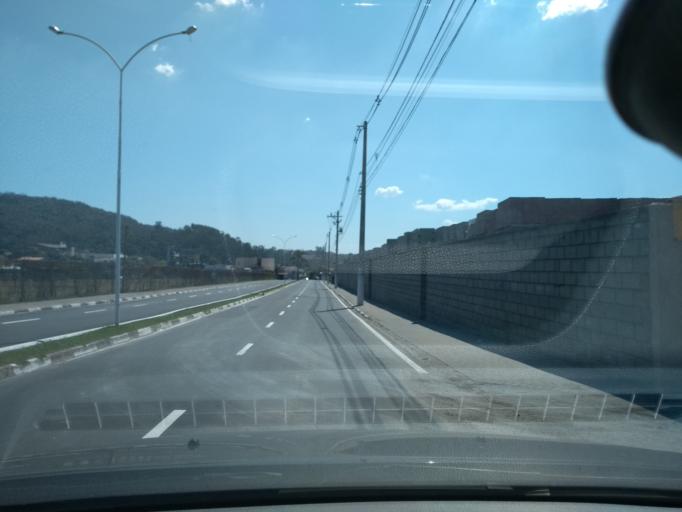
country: BR
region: Sao Paulo
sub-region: Itupeva
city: Itupeva
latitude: -23.1535
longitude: -47.0495
